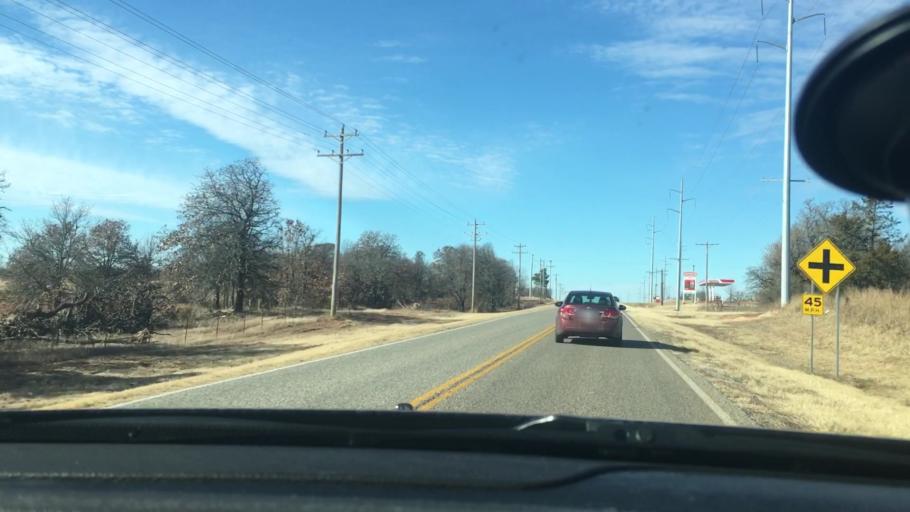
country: US
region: Oklahoma
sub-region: Cleveland County
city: Lexington
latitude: 35.0150
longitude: -97.2092
